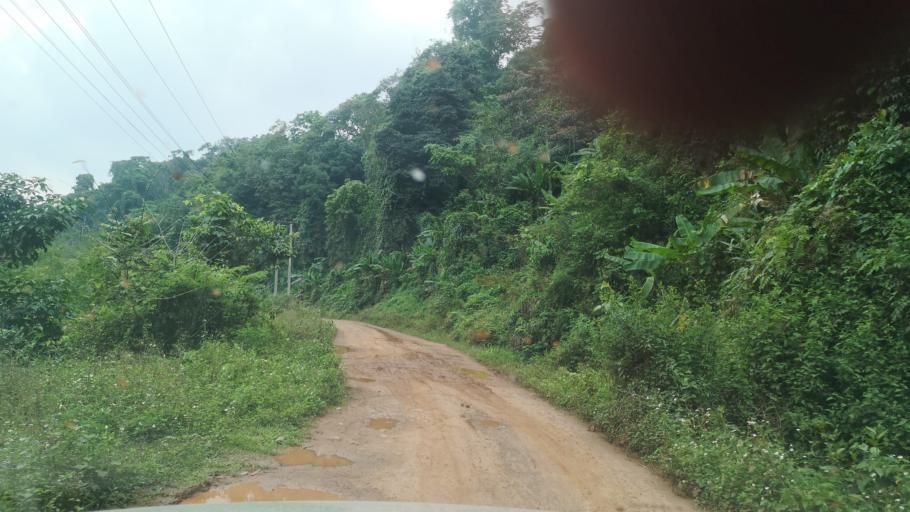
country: LA
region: Oudomxai
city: Muang La
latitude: 21.0765
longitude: 101.8468
